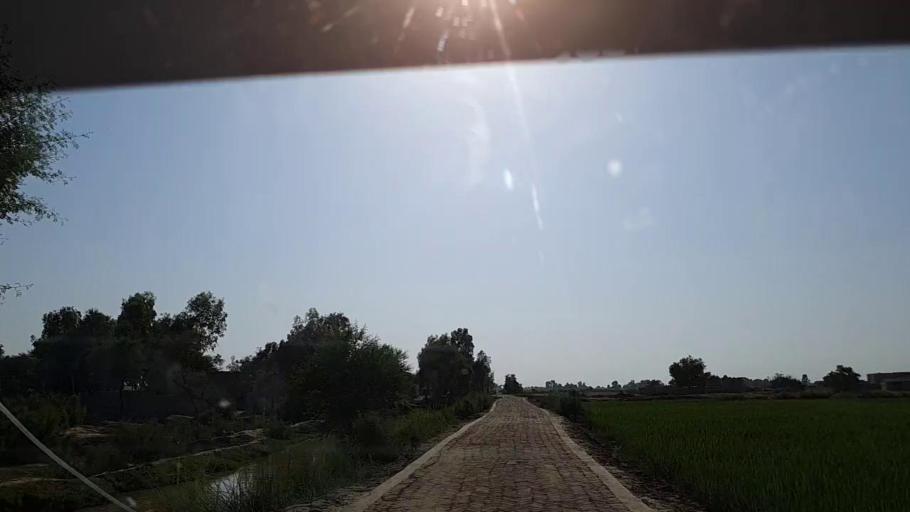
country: PK
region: Sindh
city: Tangwani
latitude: 28.2141
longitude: 68.9637
